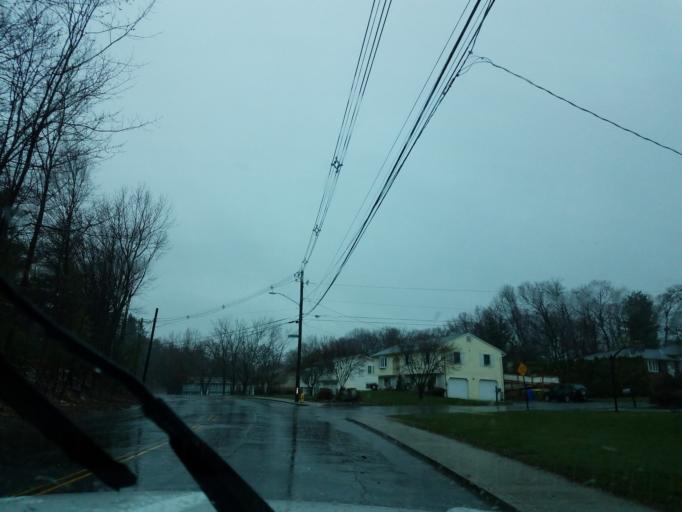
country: US
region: Connecticut
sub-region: New Haven County
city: Waterbury
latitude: 41.5385
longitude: -73.0660
